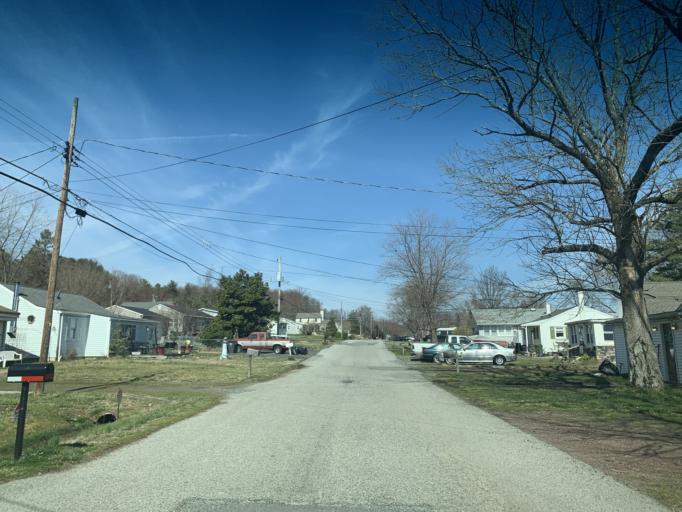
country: US
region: Maryland
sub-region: Cecil County
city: Charlestown
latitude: 39.5423
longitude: -76.0055
